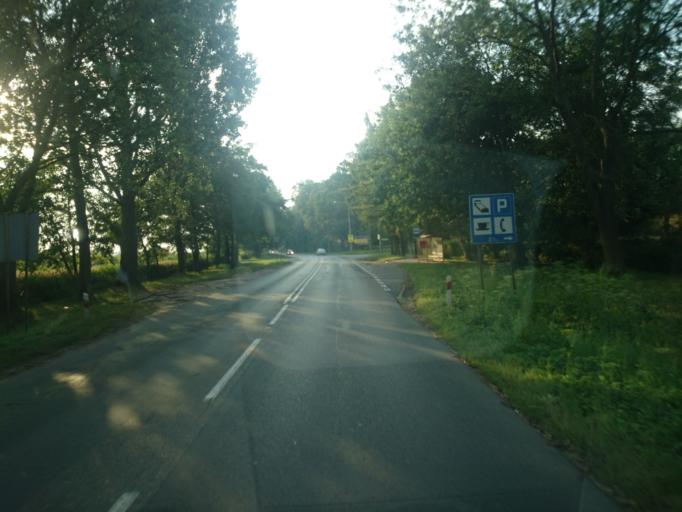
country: PL
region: Lubusz
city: Gorzow Wielkopolski
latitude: 52.7425
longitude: 15.1712
